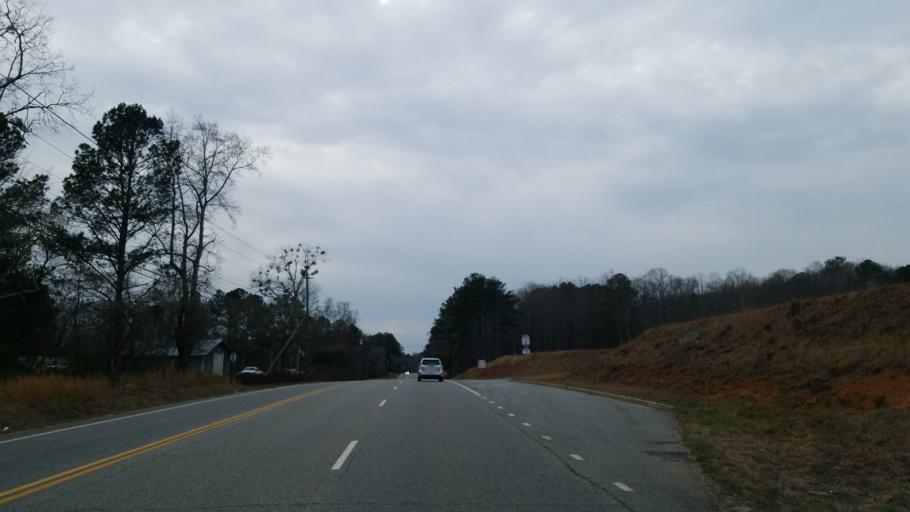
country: US
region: Georgia
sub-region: Cherokee County
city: Canton
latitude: 34.2822
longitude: -84.4405
